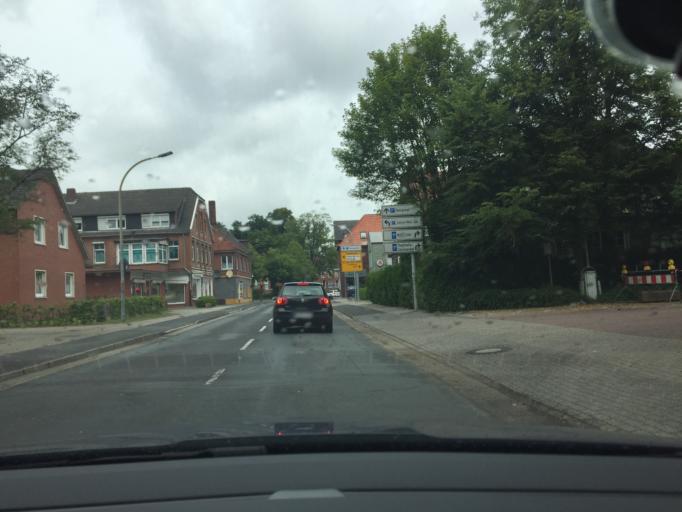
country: DE
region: Lower Saxony
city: Aurich
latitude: 53.4661
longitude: 7.4807
